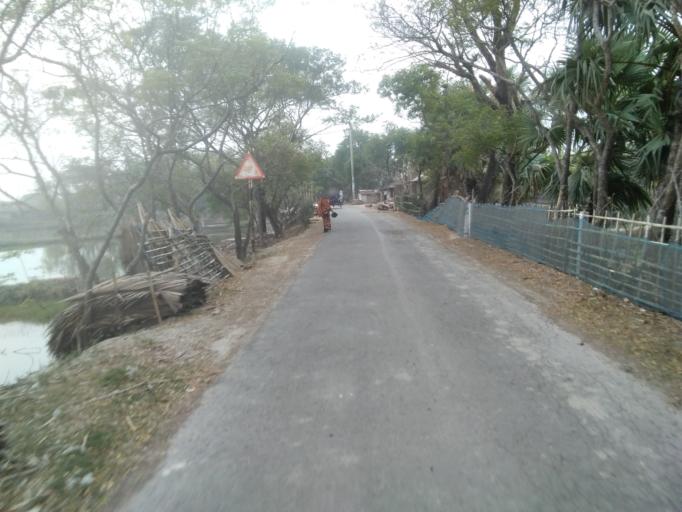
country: BD
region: Khulna
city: Satkhira
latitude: 22.5784
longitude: 89.0709
